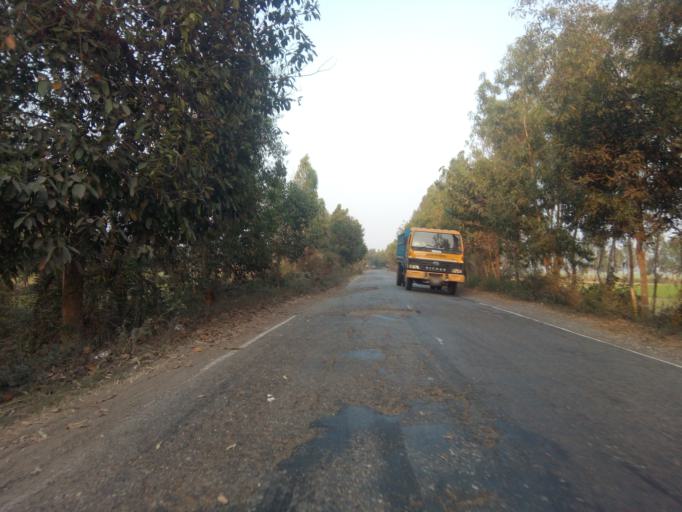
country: BD
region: Rajshahi
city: Bogra
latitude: 24.5692
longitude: 89.2128
